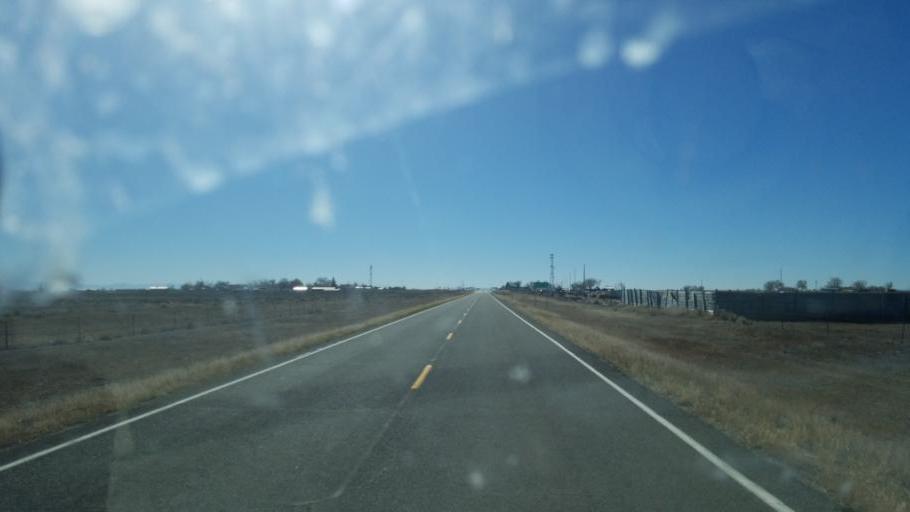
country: US
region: Colorado
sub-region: Saguache County
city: Center
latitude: 37.7557
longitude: -105.8815
